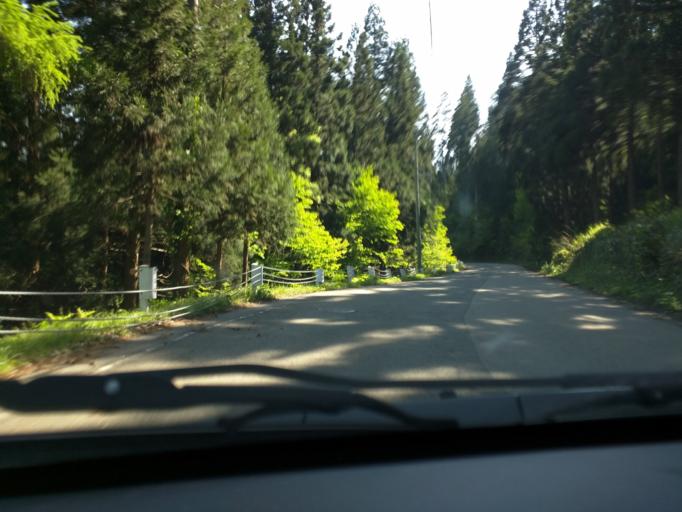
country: JP
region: Fukushima
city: Kitakata
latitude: 37.5595
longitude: 139.6261
